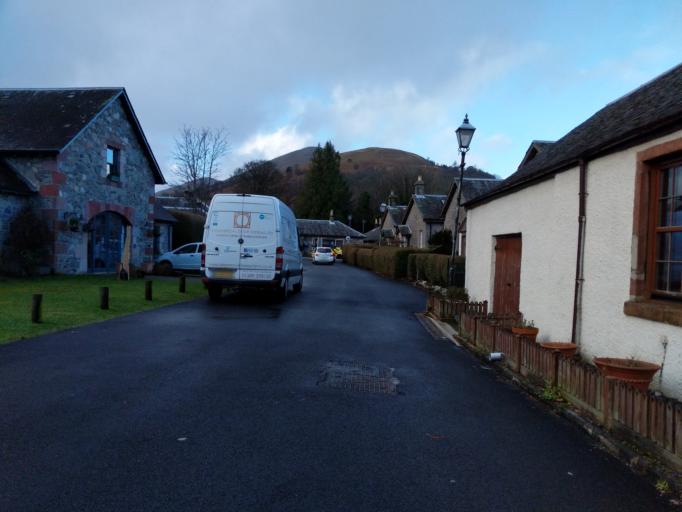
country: GB
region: Scotland
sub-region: West Dunbartonshire
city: Balloch
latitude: 56.1011
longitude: -4.6369
